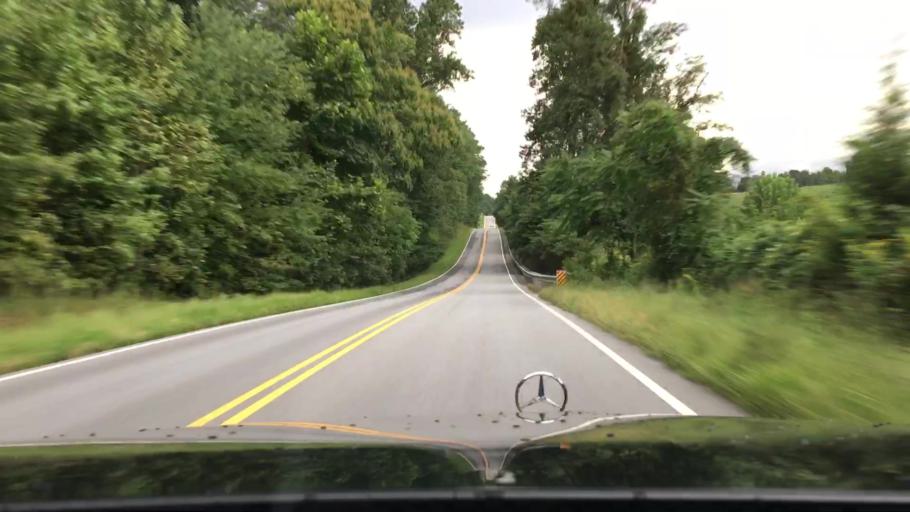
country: US
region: Virginia
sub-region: Nelson County
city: Lovingston
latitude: 37.8090
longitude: -78.9459
